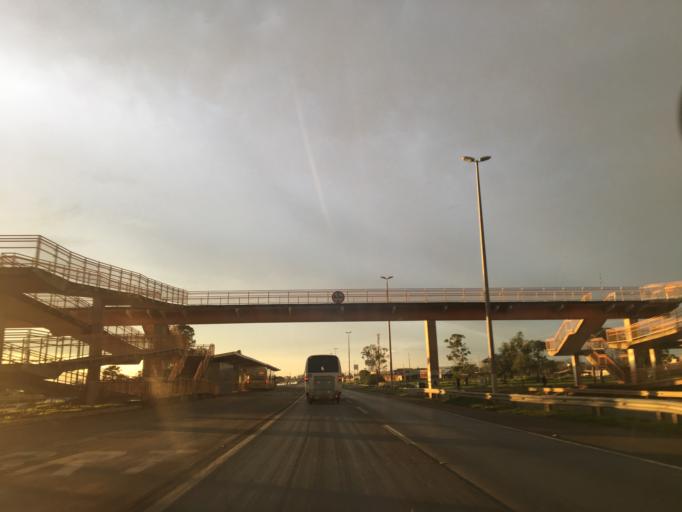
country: BR
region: Federal District
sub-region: Brasilia
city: Brasilia
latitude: -15.9914
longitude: -47.9866
